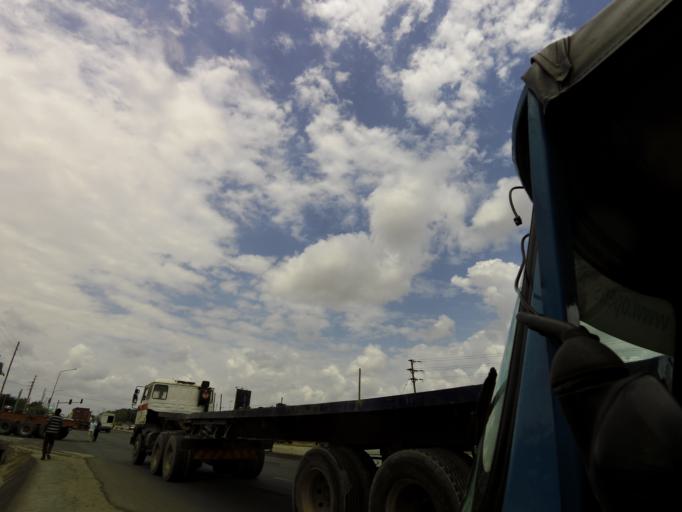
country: TZ
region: Dar es Salaam
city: Dar es Salaam
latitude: -6.8563
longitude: 39.2796
